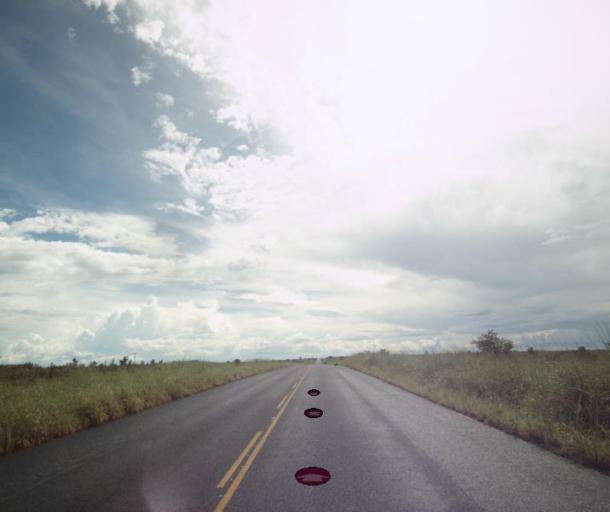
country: BR
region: Goias
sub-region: Sao Miguel Do Araguaia
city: Sao Miguel do Araguaia
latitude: -13.2961
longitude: -50.3537
